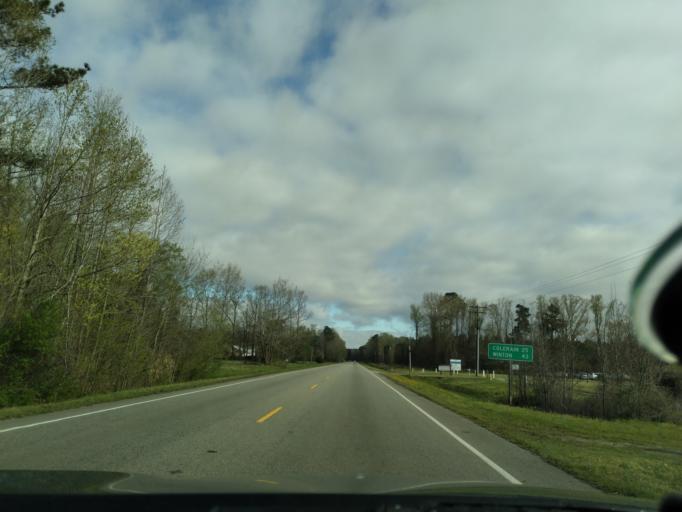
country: US
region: North Carolina
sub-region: Washington County
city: Plymouth
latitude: 35.8737
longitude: -76.6943
